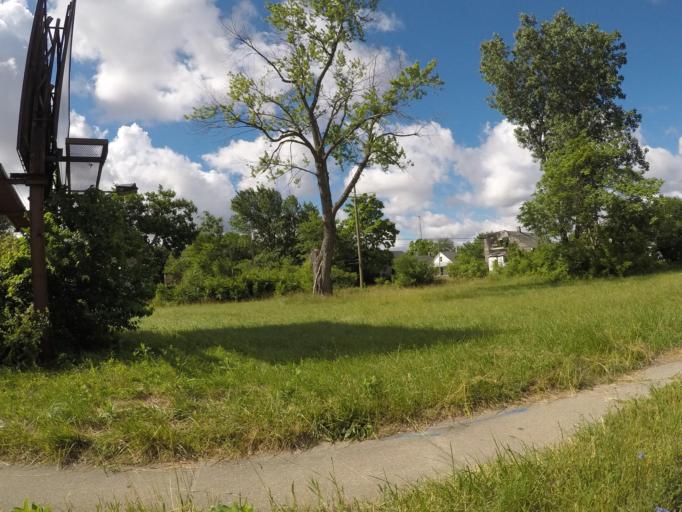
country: US
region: Michigan
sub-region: Wayne County
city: Hamtramck
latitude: 42.4188
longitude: -83.0572
